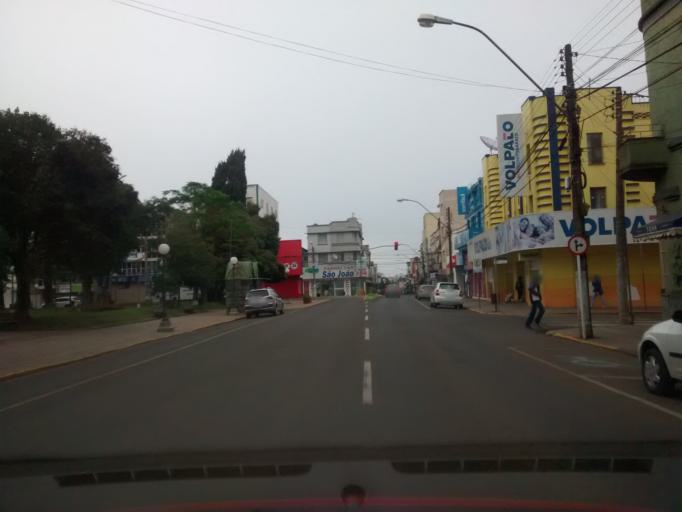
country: BR
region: Rio Grande do Sul
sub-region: Vacaria
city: Vacaria
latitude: -28.5030
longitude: -50.9379
